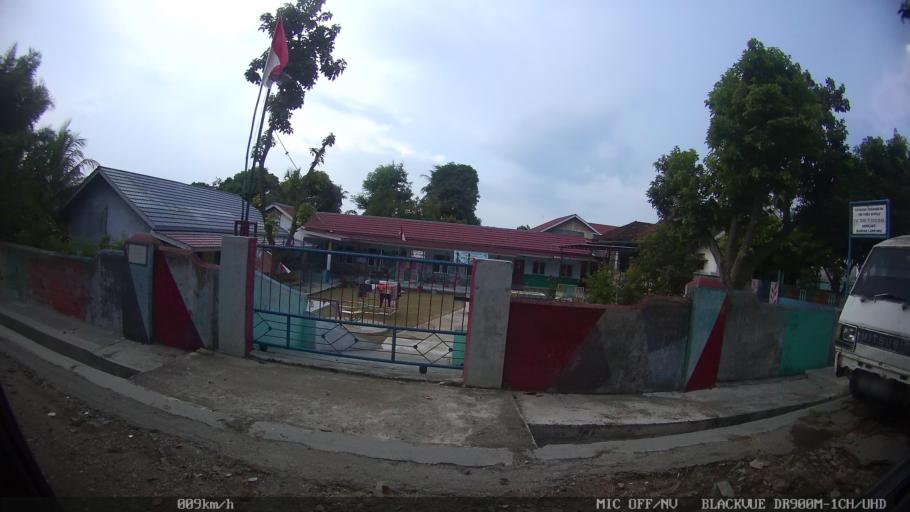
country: ID
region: Lampung
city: Kedaton
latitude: -5.3946
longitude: 105.2060
